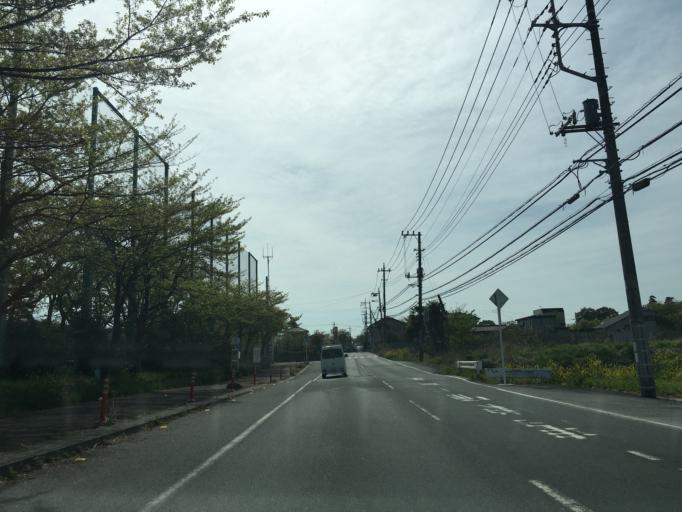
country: JP
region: Saitama
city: Ageoshimo
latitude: 35.9818
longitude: 139.6310
